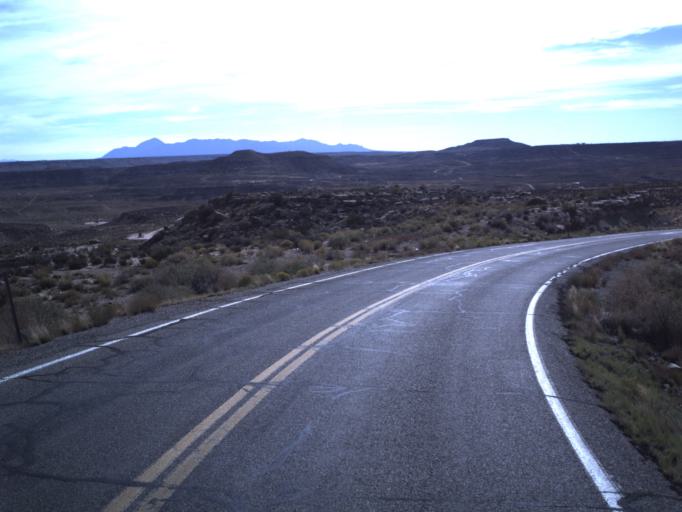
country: US
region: Utah
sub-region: San Juan County
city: Blanding
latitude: 37.3221
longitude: -109.3136
